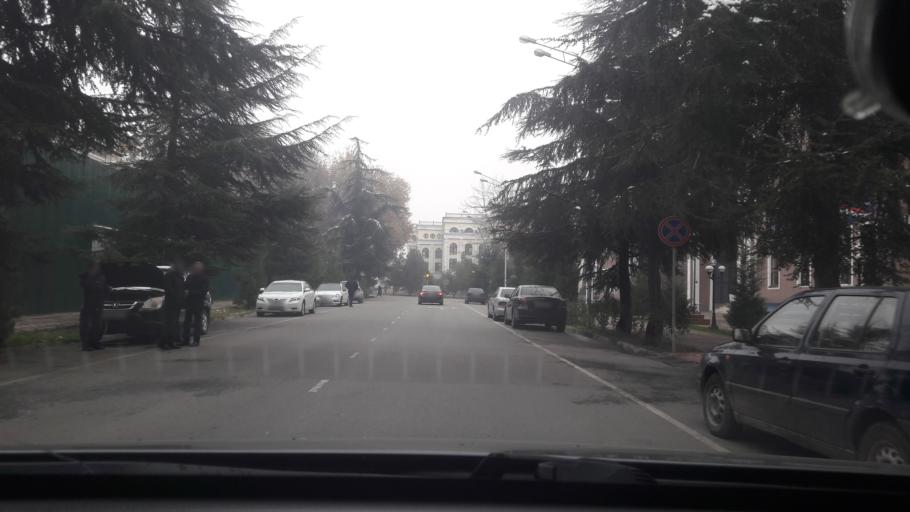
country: TJ
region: Dushanbe
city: Dushanbe
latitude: 38.5758
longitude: 68.7924
